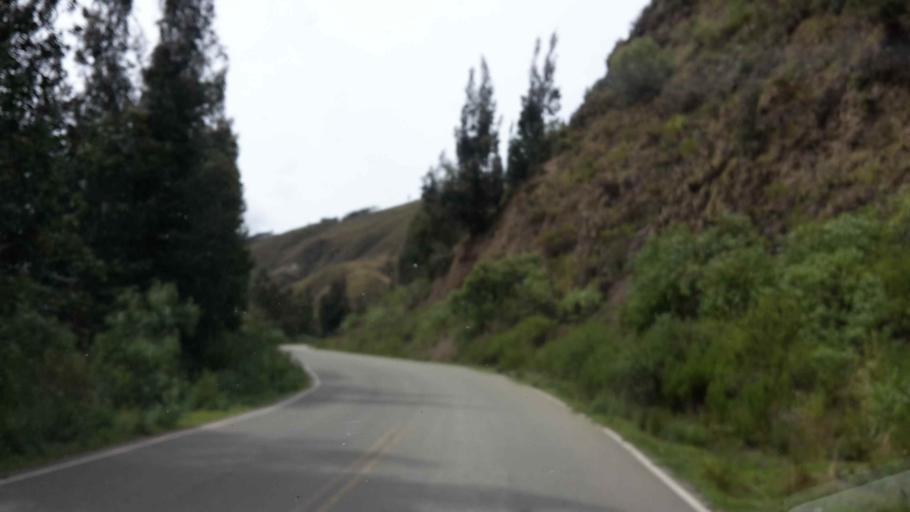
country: BO
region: Cochabamba
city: Colomi
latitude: -17.4079
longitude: -65.7876
